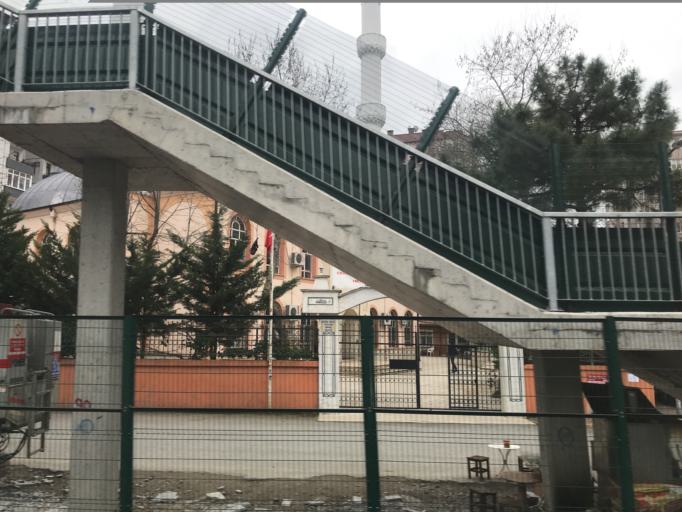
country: TR
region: Istanbul
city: Maltepe
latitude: 40.9124
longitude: 29.1530
